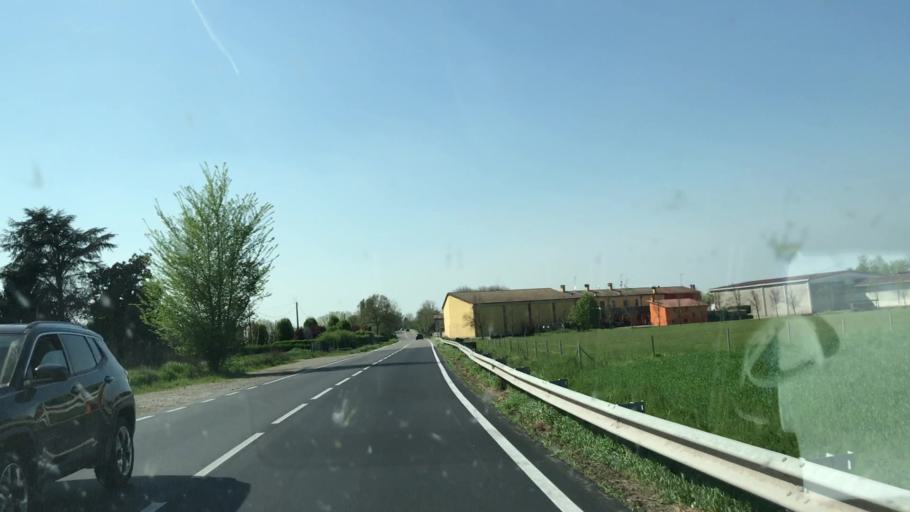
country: IT
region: Lombardy
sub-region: Provincia di Mantova
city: Marmirolo
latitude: 45.2249
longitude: 10.7321
